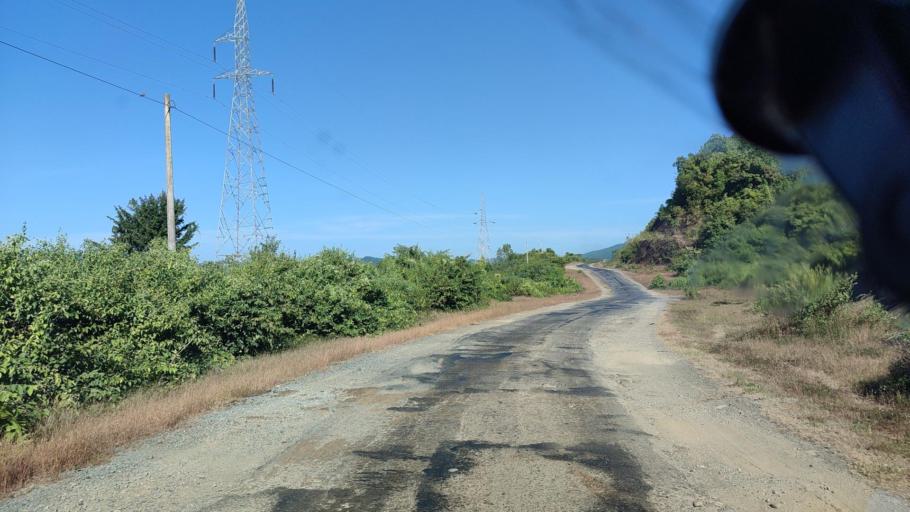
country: MM
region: Rakhine
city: Sittwe
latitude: 19.9605
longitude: 93.7298
